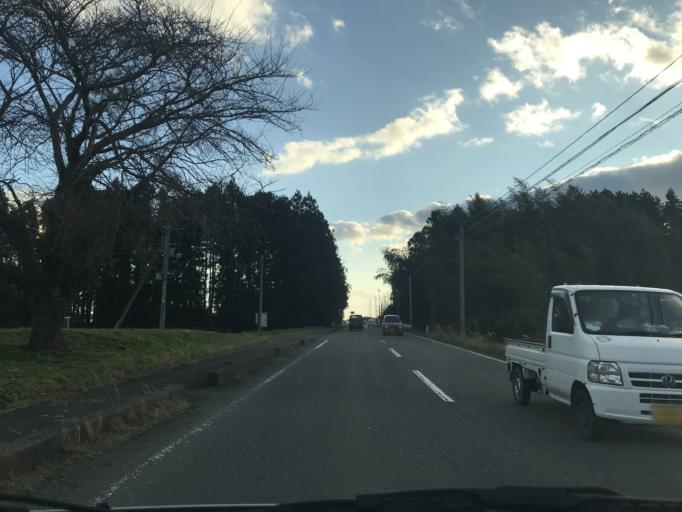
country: JP
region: Miyagi
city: Kogota
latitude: 38.6484
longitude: 141.0757
